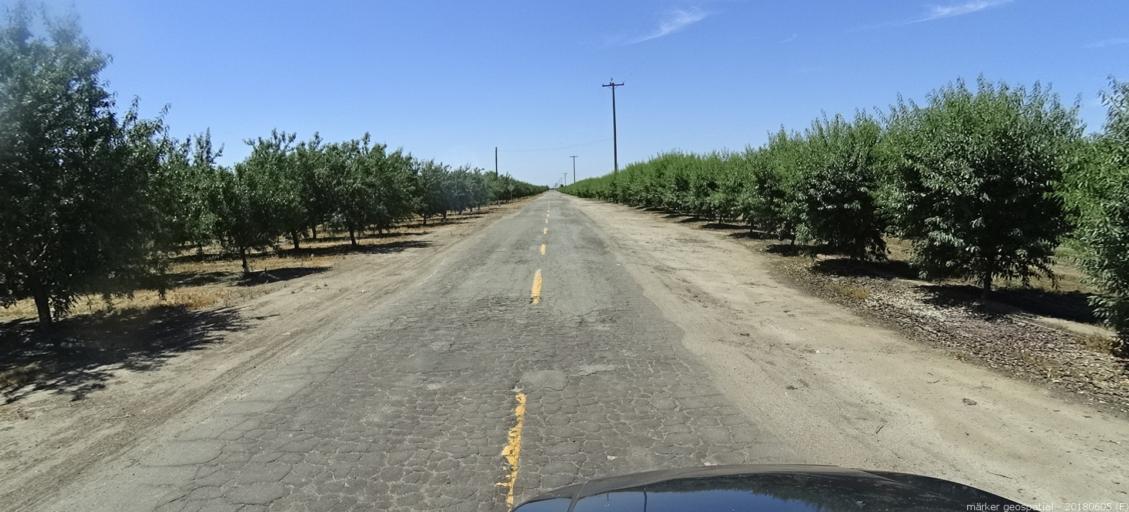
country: US
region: California
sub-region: Madera County
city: Chowchilla
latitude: 37.0970
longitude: -120.4554
